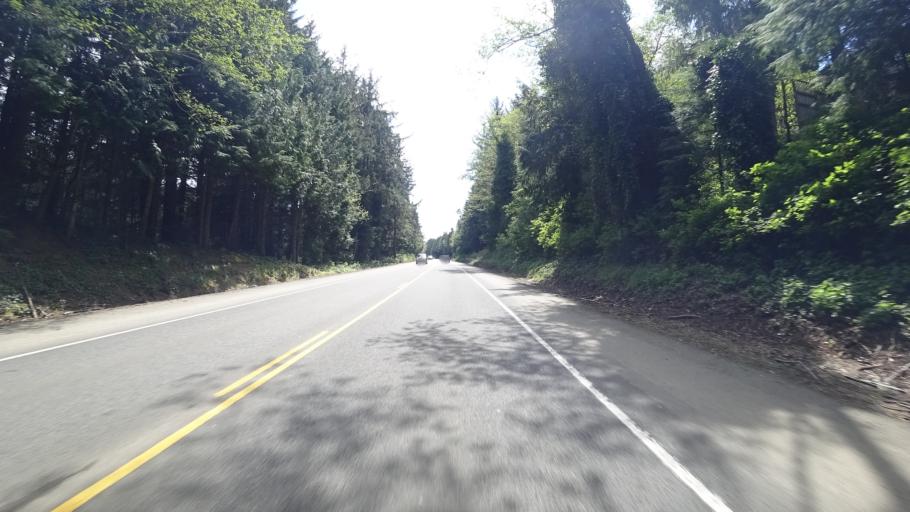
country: US
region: Oregon
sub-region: Lincoln County
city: Lincoln Beach
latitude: 44.8840
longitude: -124.0298
